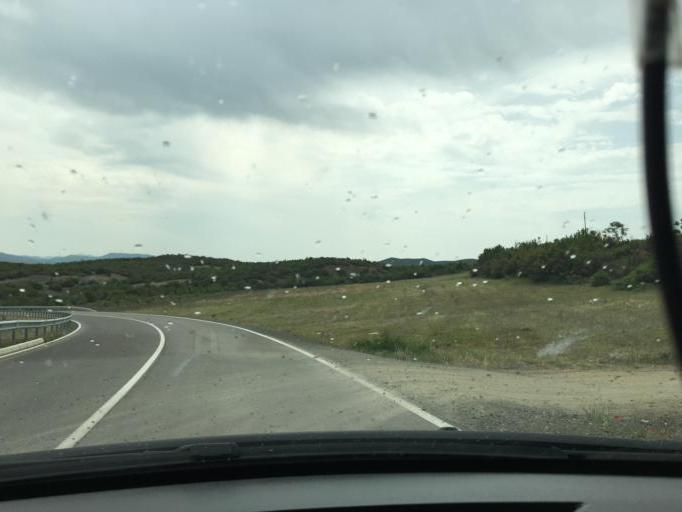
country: MK
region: Gevgelija
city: Miravci
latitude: 41.3003
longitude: 22.4370
